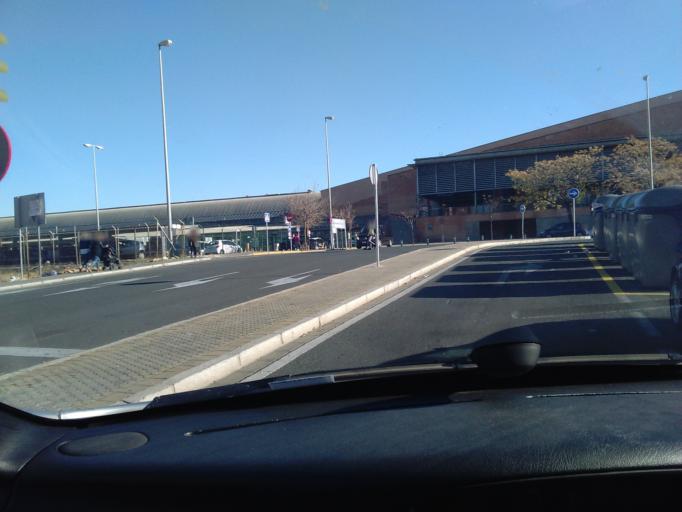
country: ES
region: Andalusia
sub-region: Provincia de Sevilla
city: Sevilla
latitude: 37.3934
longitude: -5.9761
